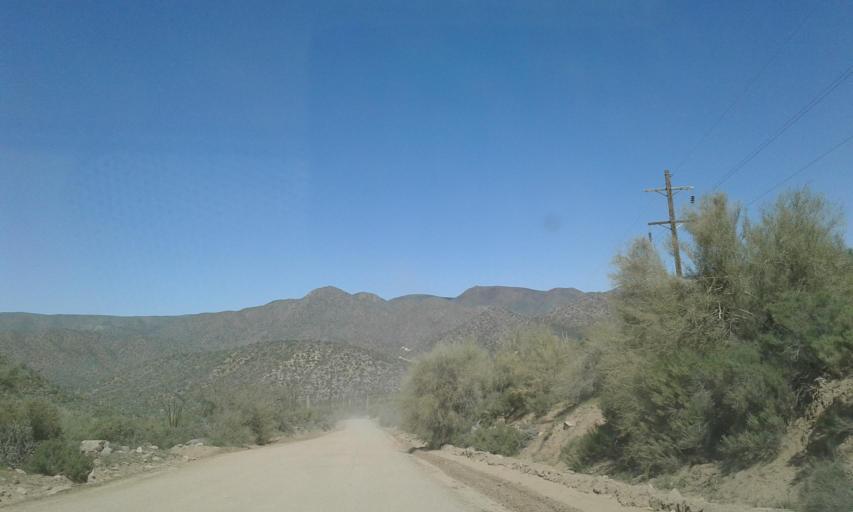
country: US
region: Arizona
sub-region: Gila County
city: Tonto Basin
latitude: 33.6145
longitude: -111.1968
